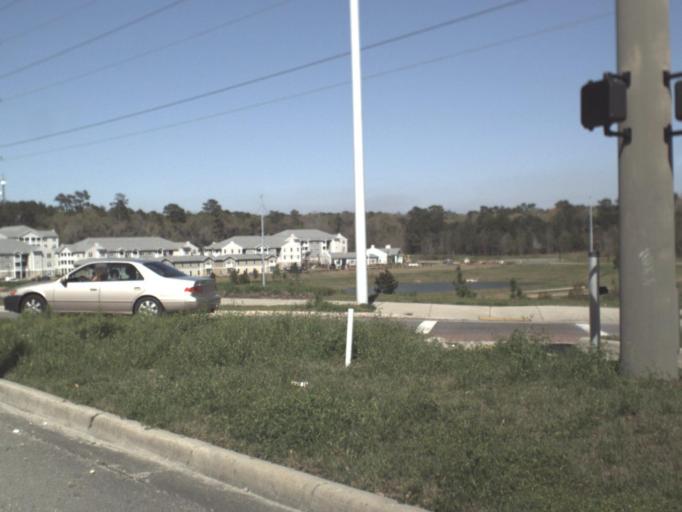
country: US
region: Florida
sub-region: Leon County
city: Tallahassee
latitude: 30.4109
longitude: -84.2348
